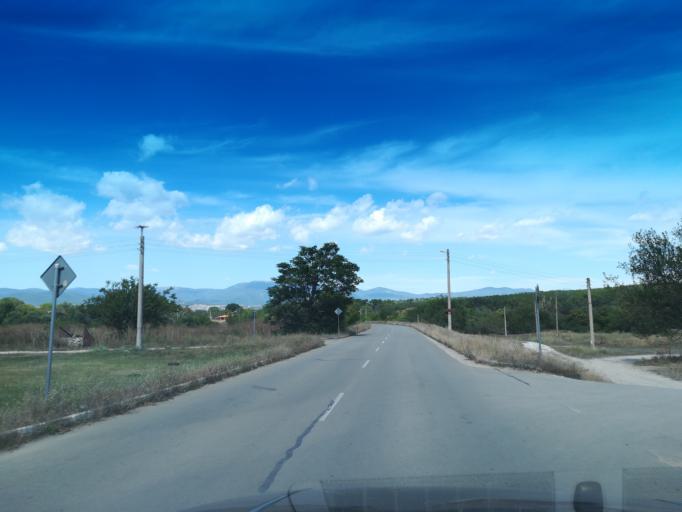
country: BG
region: Plovdiv
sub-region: Obshtina Suedinenie
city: Suedinenie
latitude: 42.4281
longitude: 24.5347
